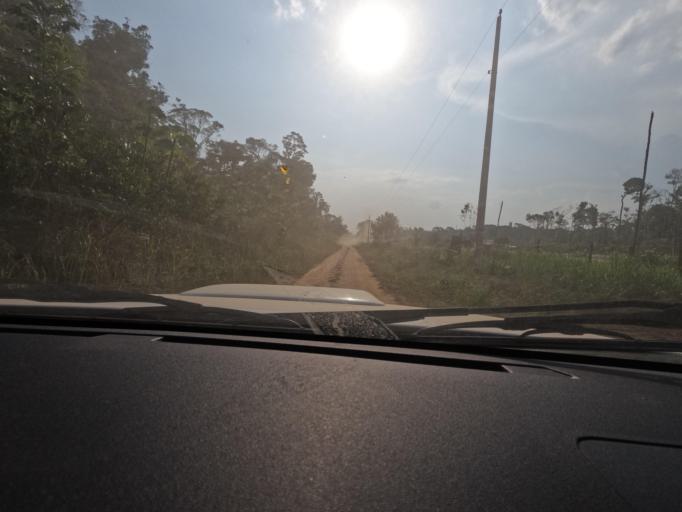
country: BR
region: Rondonia
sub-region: Porto Velho
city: Porto Velho
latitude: -8.5650
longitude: -64.0260
